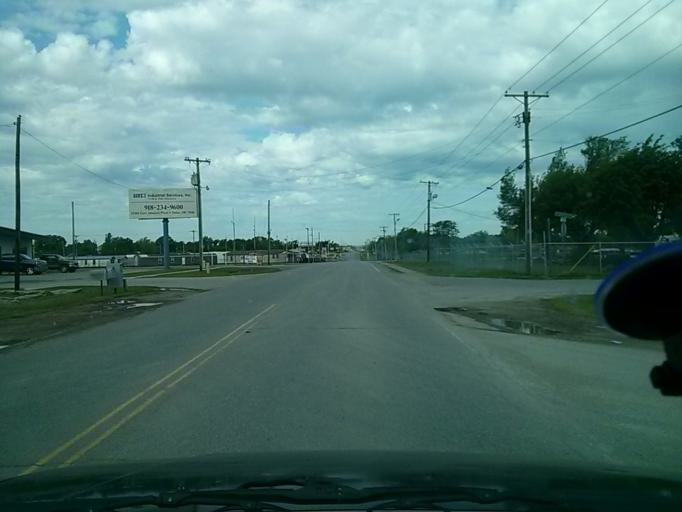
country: US
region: Oklahoma
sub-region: Rogers County
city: Catoosa
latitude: 36.1607
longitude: -95.8403
